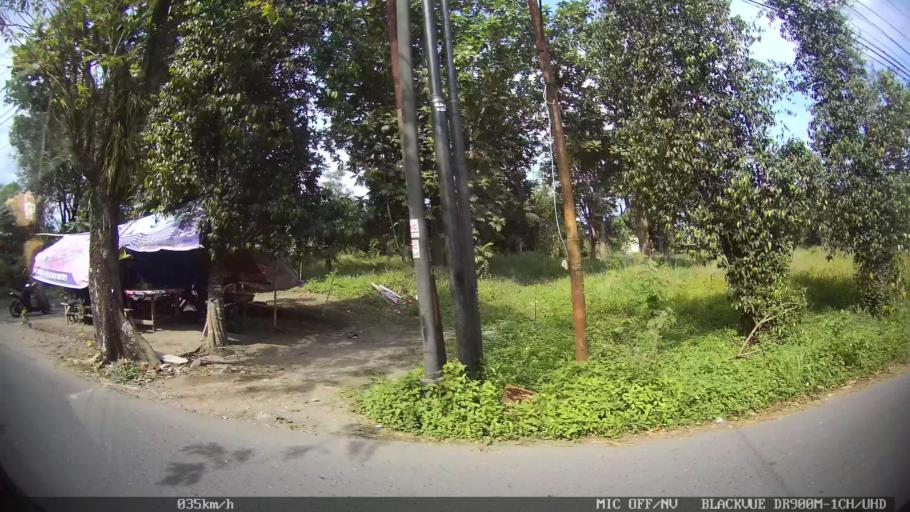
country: ID
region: Daerah Istimewa Yogyakarta
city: Depok
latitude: -7.7460
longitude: 110.4197
